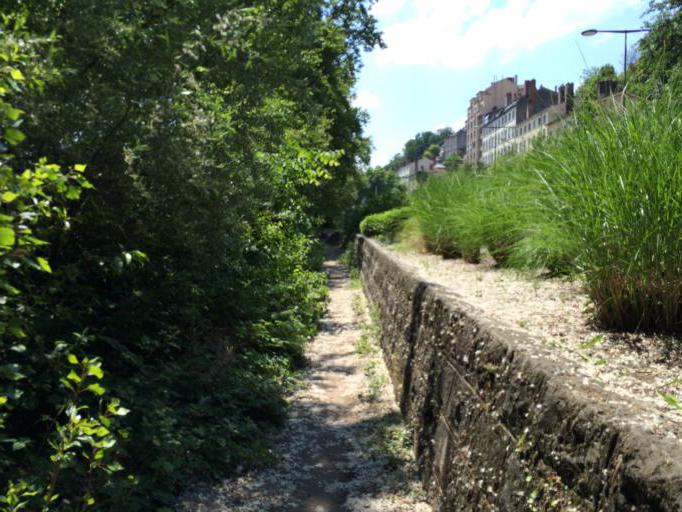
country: FR
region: Rhone-Alpes
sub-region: Departement du Rhone
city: Caluire-et-Cuire
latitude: 45.7811
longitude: 4.8427
